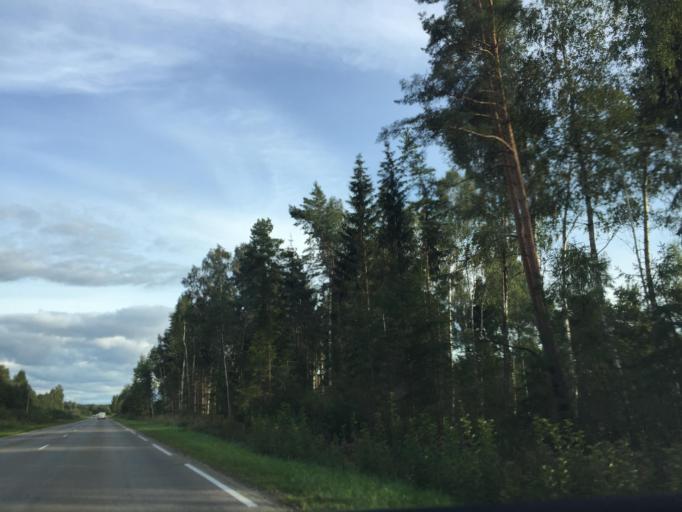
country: LV
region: Jaunjelgava
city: Jaunjelgava
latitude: 56.3568
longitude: 25.0487
